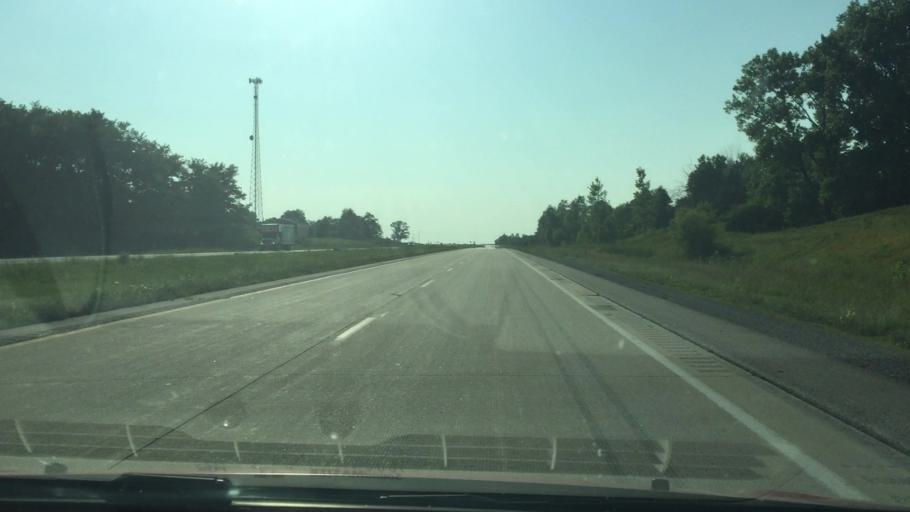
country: US
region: Iowa
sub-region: Scott County
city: Blue Grass
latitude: 41.5184
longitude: -90.8484
